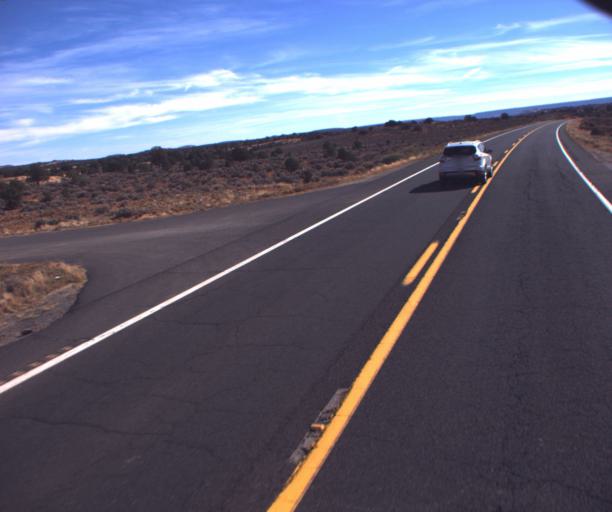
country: US
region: Arizona
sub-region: Coconino County
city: Kaibito
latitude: 36.5616
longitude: -110.7240
